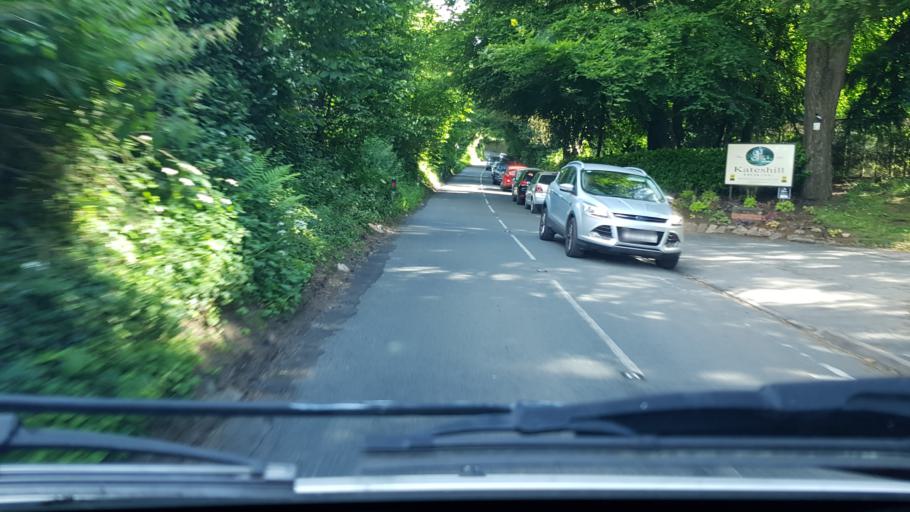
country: GB
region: England
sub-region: Worcestershire
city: Bewdley
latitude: 52.3715
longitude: -2.3124
